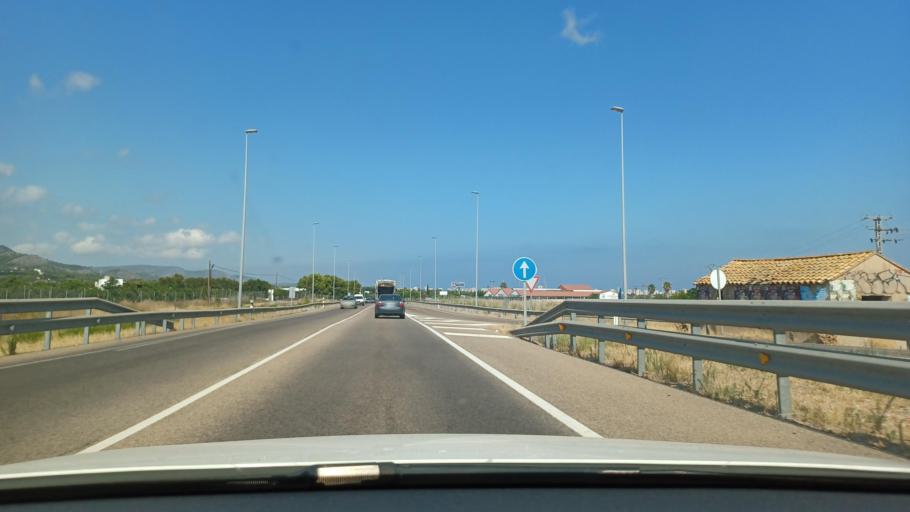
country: ES
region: Valencia
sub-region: Provincia de Castello
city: Castello de la Plana
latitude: 40.0285
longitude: 0.0015
